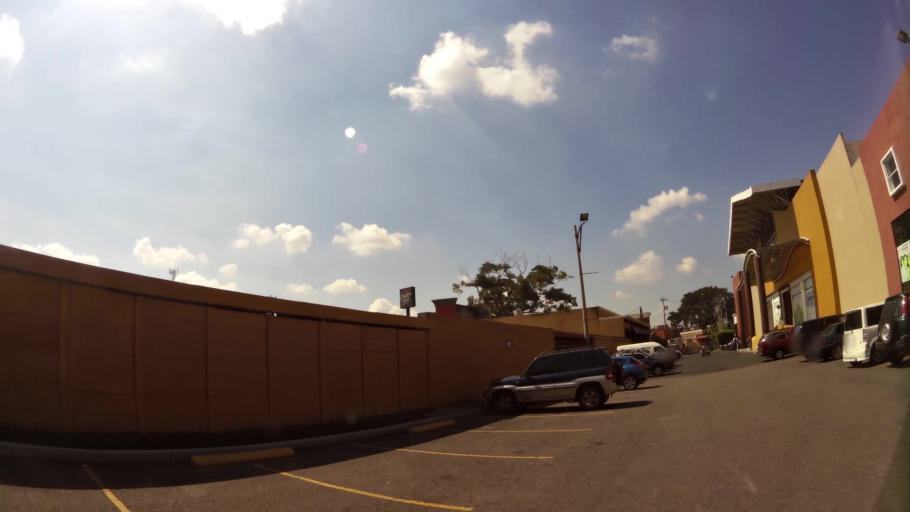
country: GT
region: Suchitepeque
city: Mazatenango
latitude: 14.5341
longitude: -91.4924
